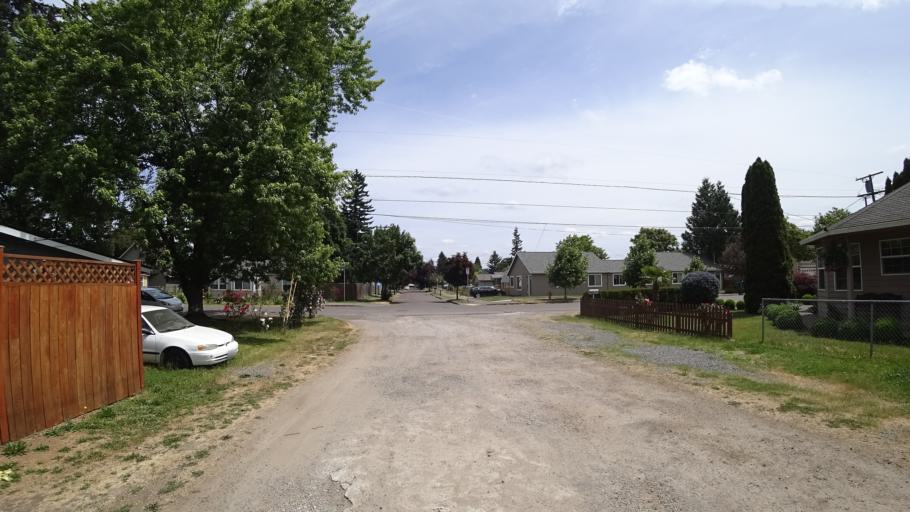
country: US
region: Oregon
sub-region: Multnomah County
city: Lents
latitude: 45.4674
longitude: -122.5982
